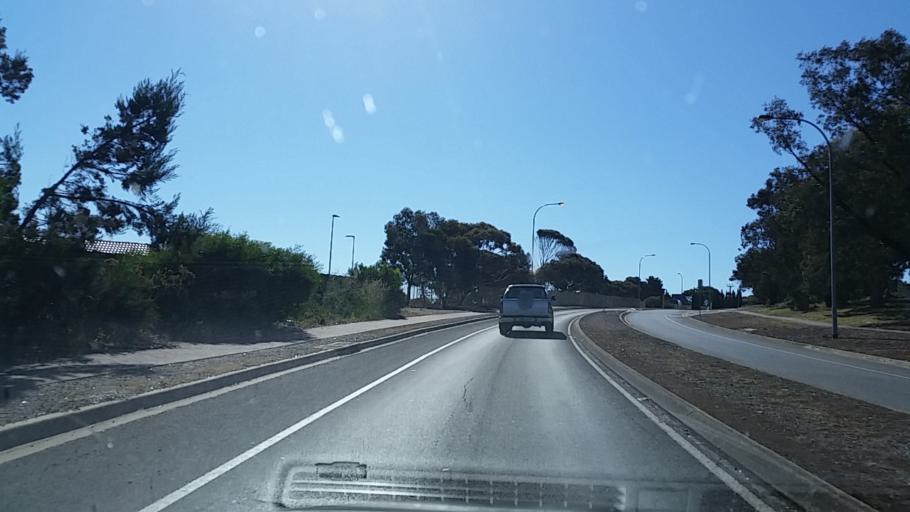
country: AU
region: South Australia
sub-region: Onkaparinga
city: Noarlunga Downs
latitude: -35.1474
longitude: 138.5015
